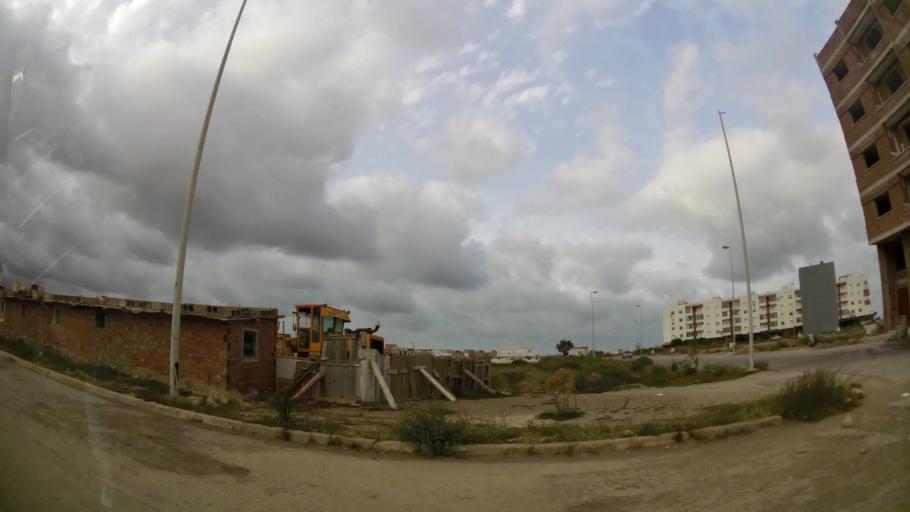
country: MA
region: Oriental
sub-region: Nador
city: Nador
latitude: 35.1545
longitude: -2.9138
